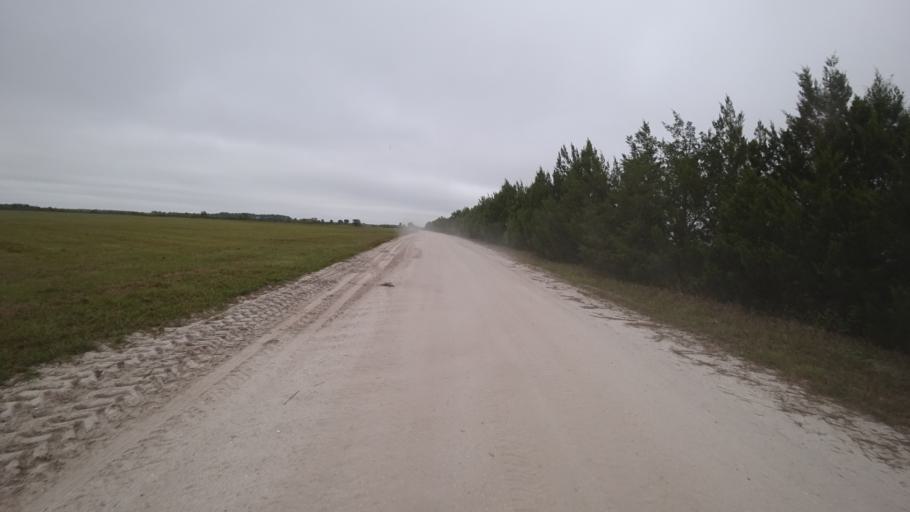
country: US
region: Florida
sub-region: Sarasota County
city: Warm Mineral Springs
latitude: 27.2962
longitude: -82.1346
